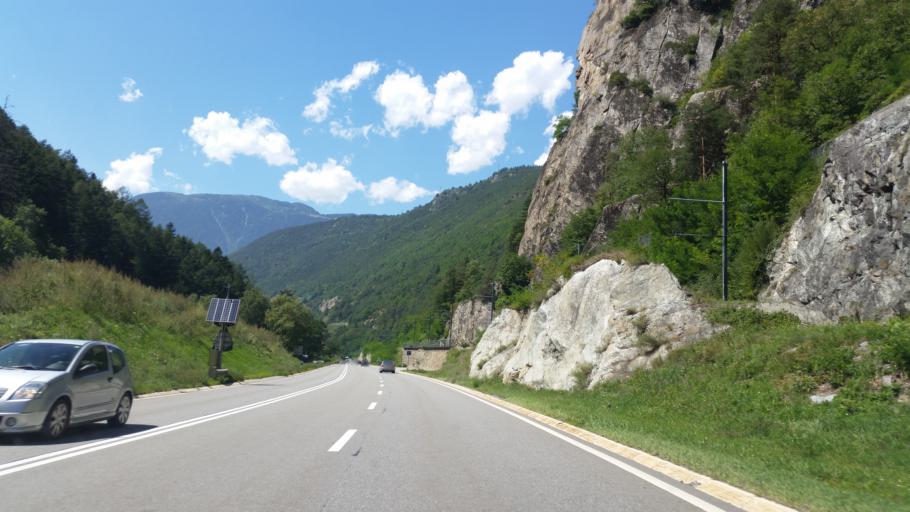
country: CH
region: Valais
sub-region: Martigny District
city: Martigny-Ville
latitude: 46.0818
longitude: 7.1055
